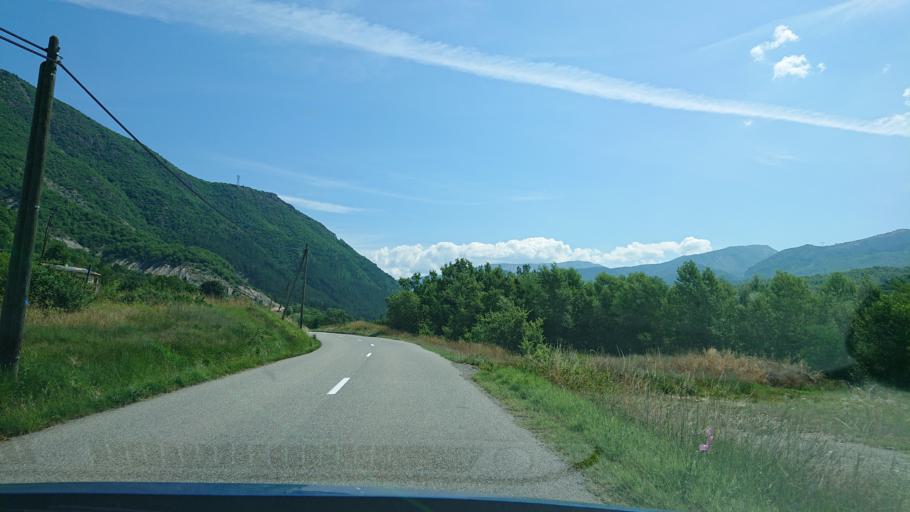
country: FR
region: Provence-Alpes-Cote d'Azur
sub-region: Departement des Alpes-de-Haute-Provence
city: Sisteron
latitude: 44.2619
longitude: 5.9762
